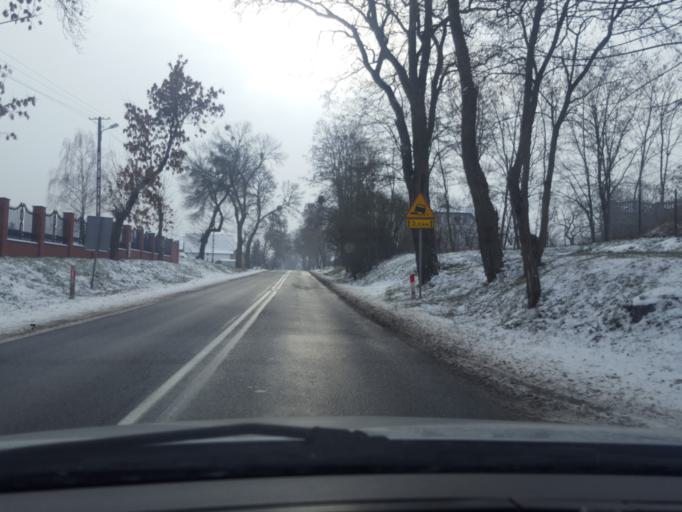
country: PL
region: Lodz Voivodeship
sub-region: Powiat brzezinski
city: Rogow
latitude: 51.8603
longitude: 19.8175
